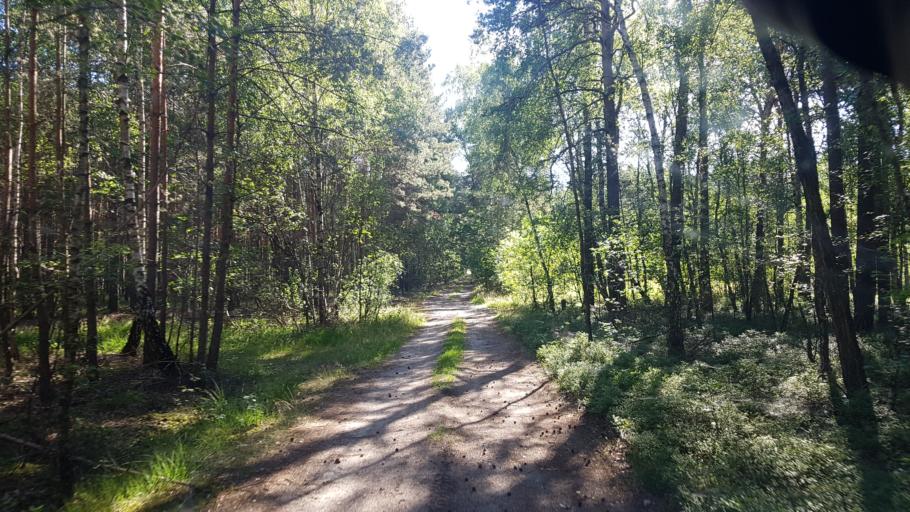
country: DE
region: Brandenburg
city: Sallgast
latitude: 51.6046
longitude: 13.8242
